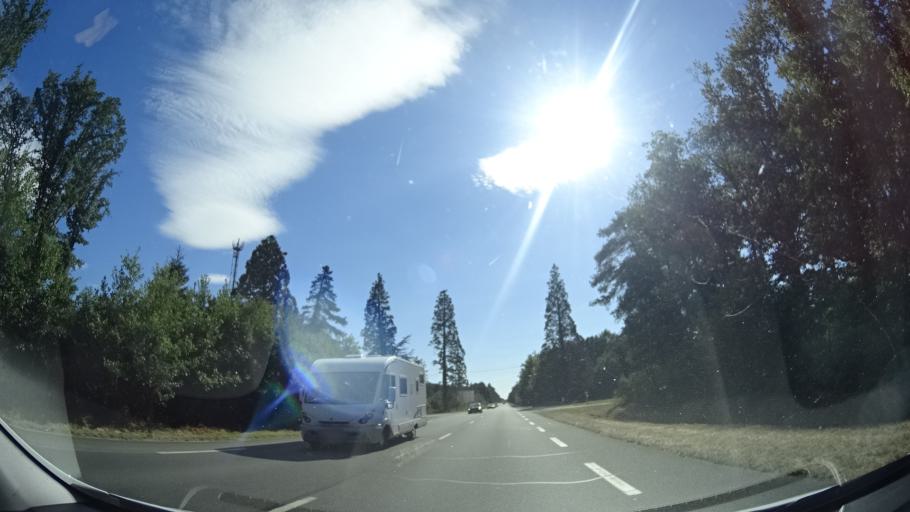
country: FR
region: Centre
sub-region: Departement du Loiret
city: Vitry-aux-Loges
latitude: 47.9143
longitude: 2.3095
